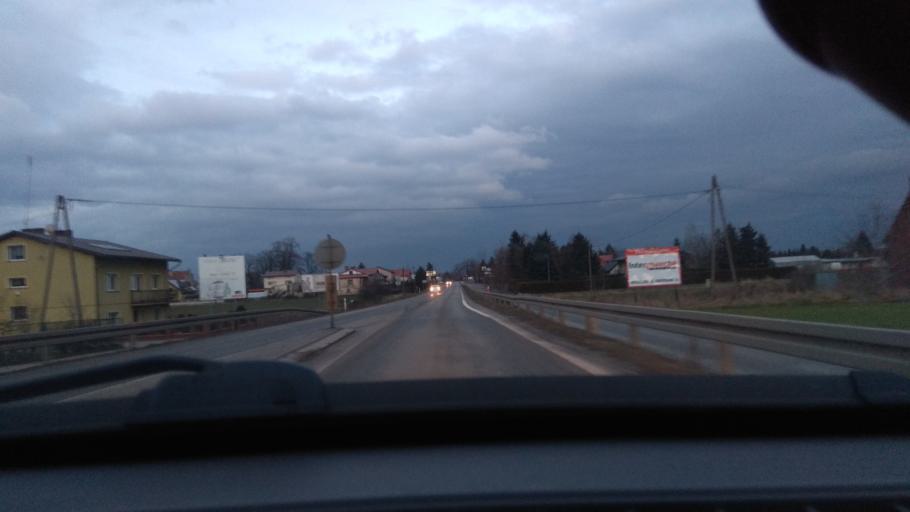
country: PL
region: Greater Poland Voivodeship
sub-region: Powiat kepinski
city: Baranow
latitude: 51.2920
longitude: 18.0285
